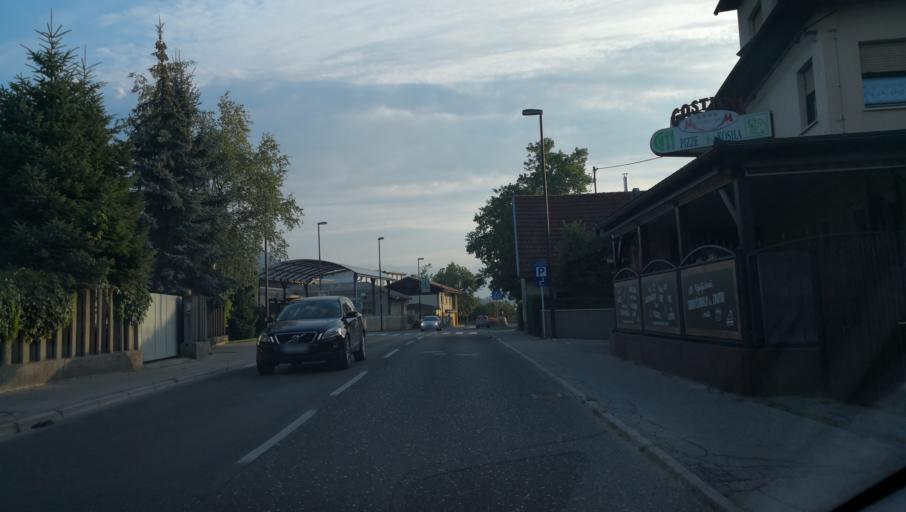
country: SI
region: Medvode
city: Zgornje Pirnice
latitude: 46.1040
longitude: 14.4627
